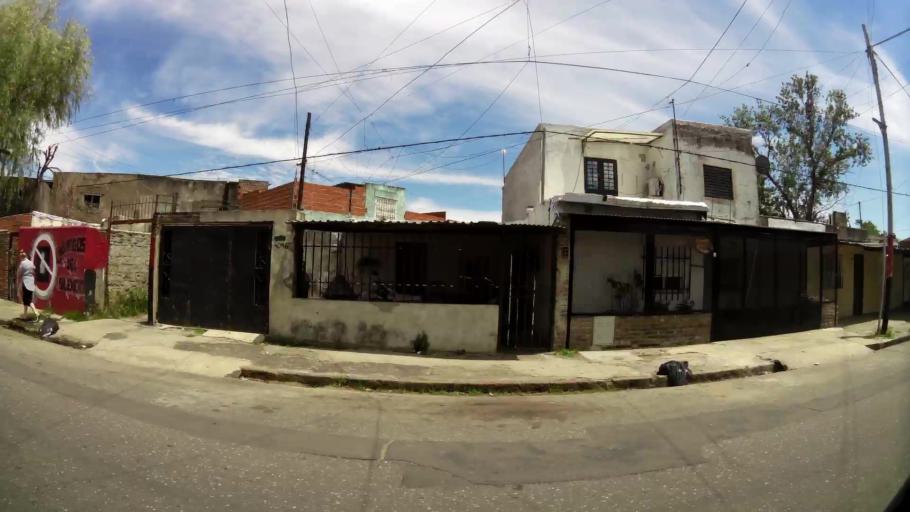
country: AR
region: Santa Fe
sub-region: Departamento de Rosario
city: Rosario
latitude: -32.9866
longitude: -60.6363
